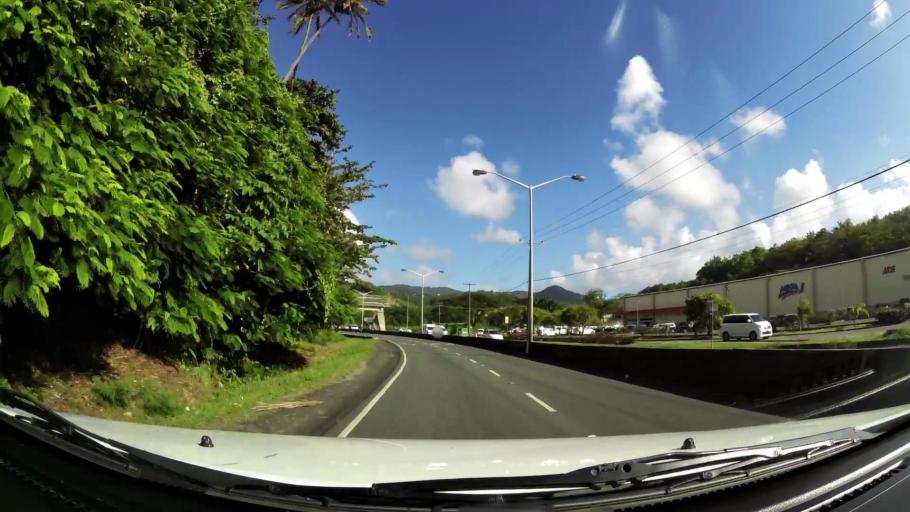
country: LC
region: Castries Quarter
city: Bisee
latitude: 14.0347
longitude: -60.9711
